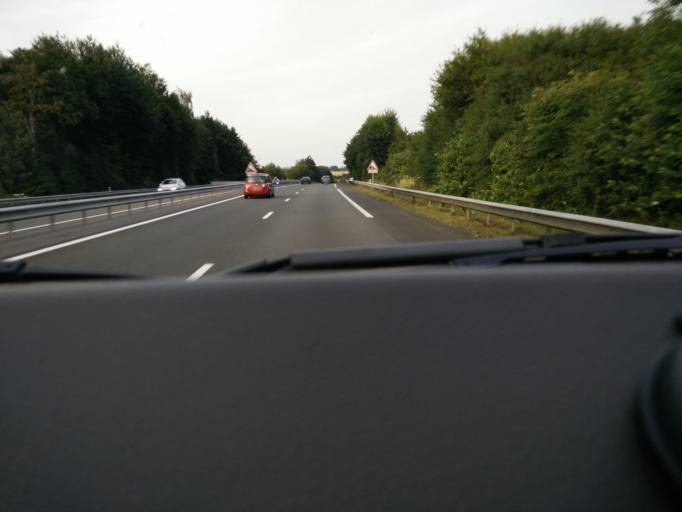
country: FR
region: Nord-Pas-de-Calais
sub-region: Departement du Nord
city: Gommegnies
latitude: 50.3063
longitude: 3.7381
